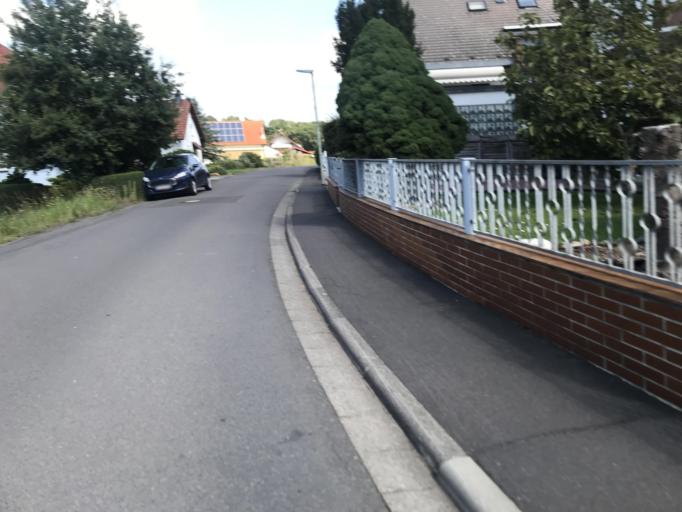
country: DE
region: Hesse
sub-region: Regierungsbezirk Darmstadt
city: Echzell
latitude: 50.4277
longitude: 8.9169
